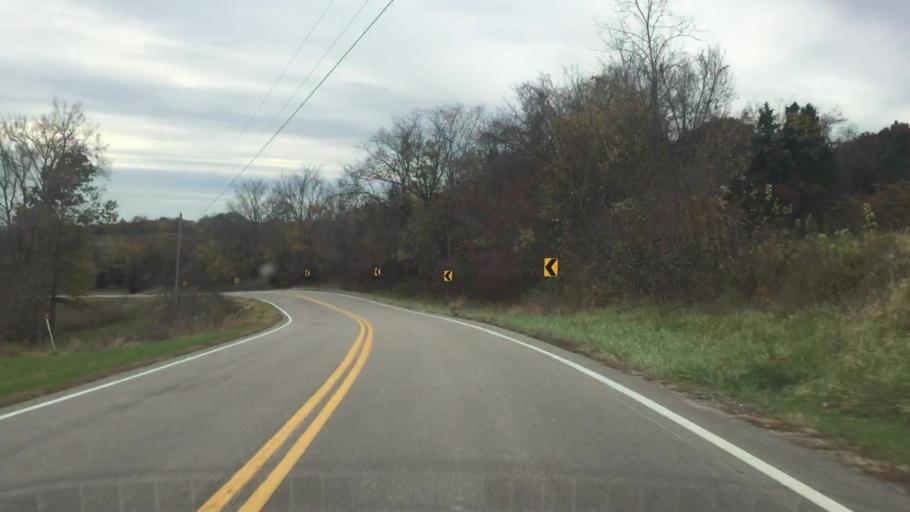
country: US
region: Missouri
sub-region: Callaway County
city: Fulton
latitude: 38.7126
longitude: -91.7366
